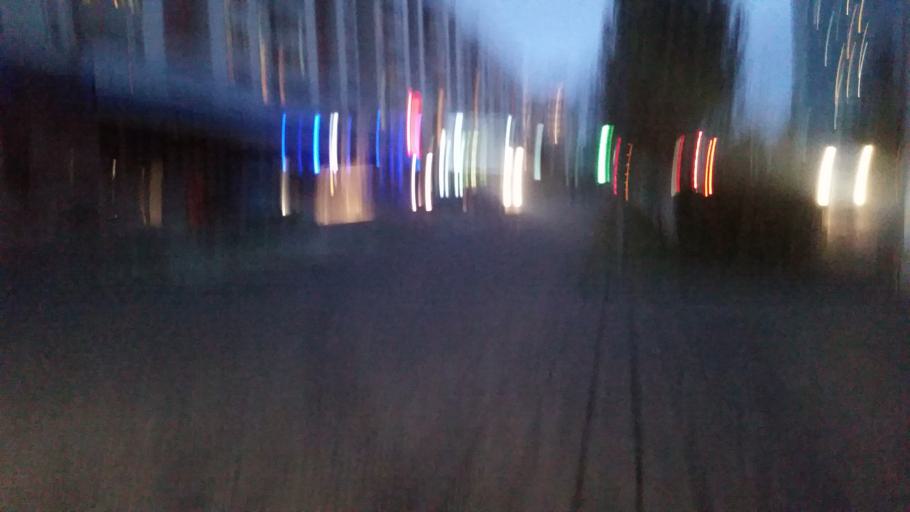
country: KZ
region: Astana Qalasy
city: Astana
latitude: 51.1262
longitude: 71.4274
